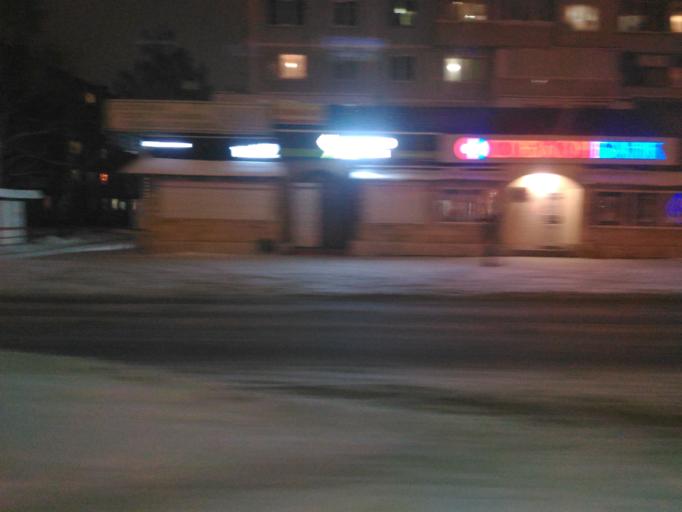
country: RU
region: Ulyanovsk
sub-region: Ulyanovskiy Rayon
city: Ulyanovsk
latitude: 54.3207
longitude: 48.3573
